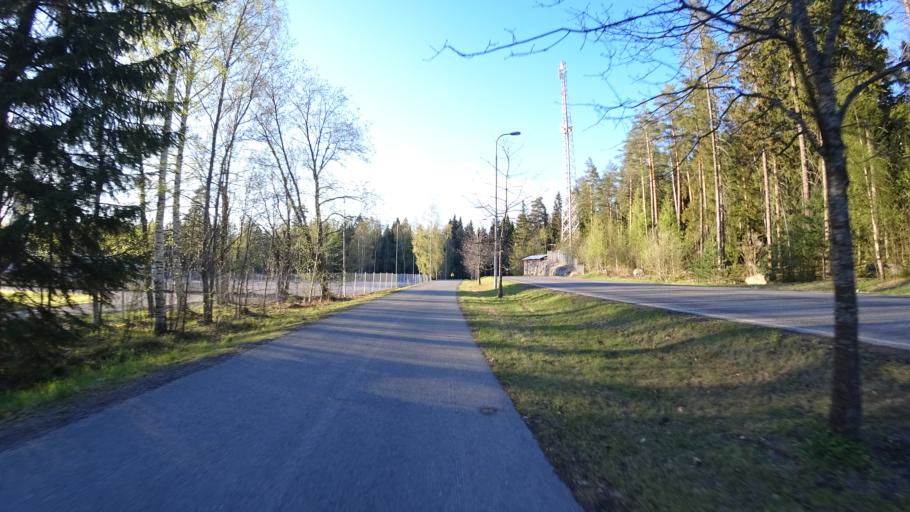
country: FI
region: Pirkanmaa
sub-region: Tampere
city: Pirkkala
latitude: 61.5034
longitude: 23.6106
